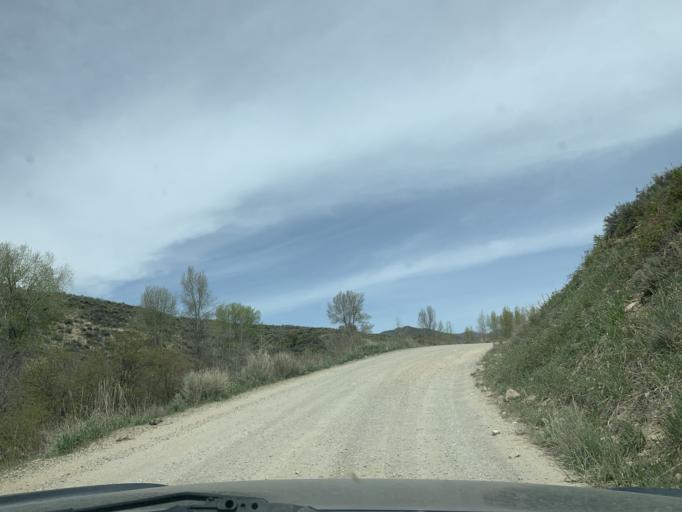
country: US
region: Utah
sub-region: Utah County
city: Mapleton
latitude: 40.1739
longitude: -111.3305
